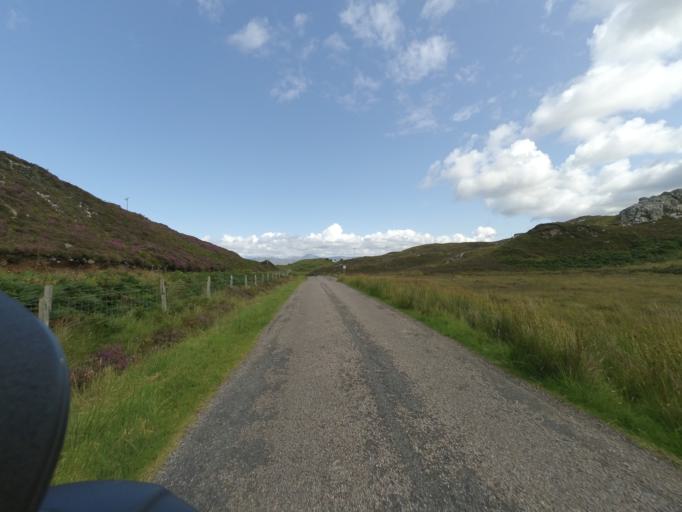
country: GB
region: Scotland
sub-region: Highland
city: Ullapool
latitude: 58.2414
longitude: -5.1949
